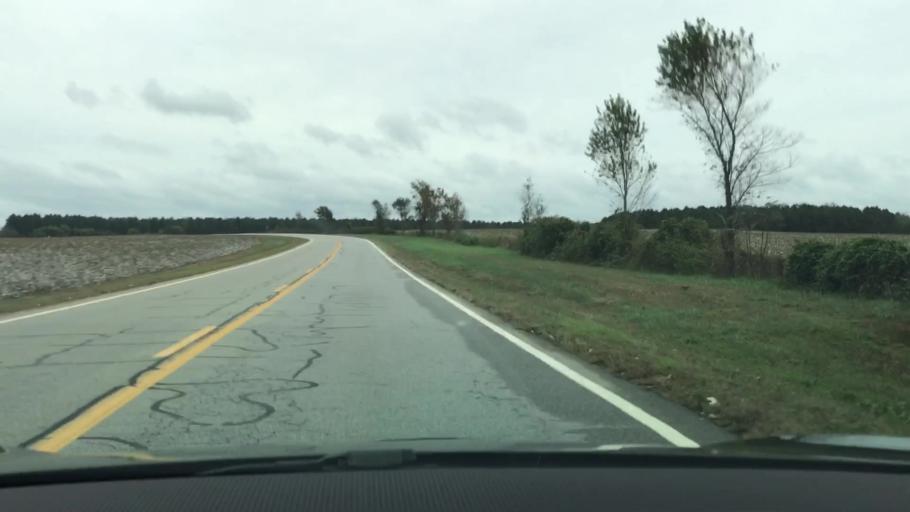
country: US
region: Georgia
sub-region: Warren County
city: Warrenton
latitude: 33.3593
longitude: -82.5960
